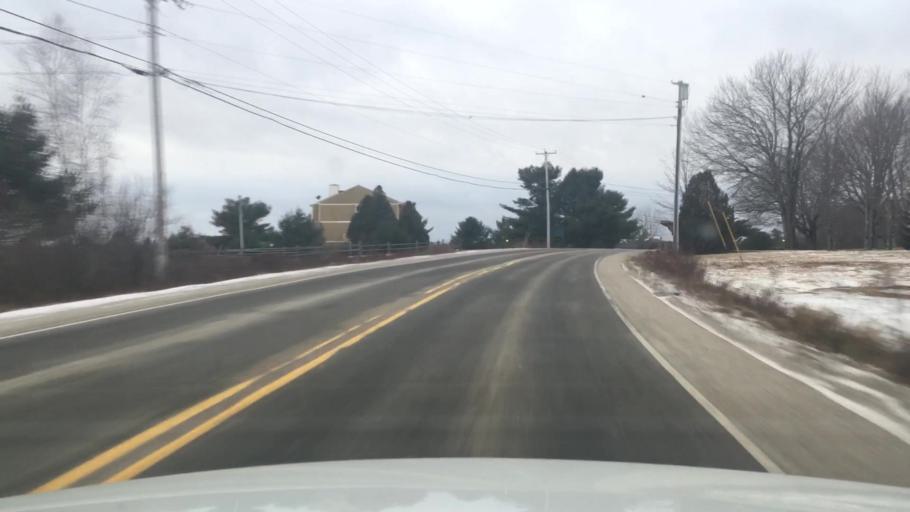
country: US
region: Maine
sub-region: Hancock County
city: Trenton
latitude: 44.4896
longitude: -68.3656
